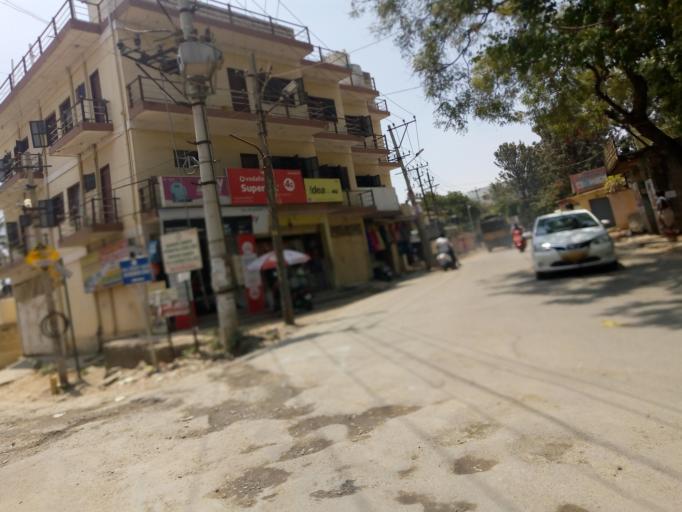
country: IN
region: Karnataka
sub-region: Bangalore Urban
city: Bangalore
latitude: 12.8896
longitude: 77.6566
